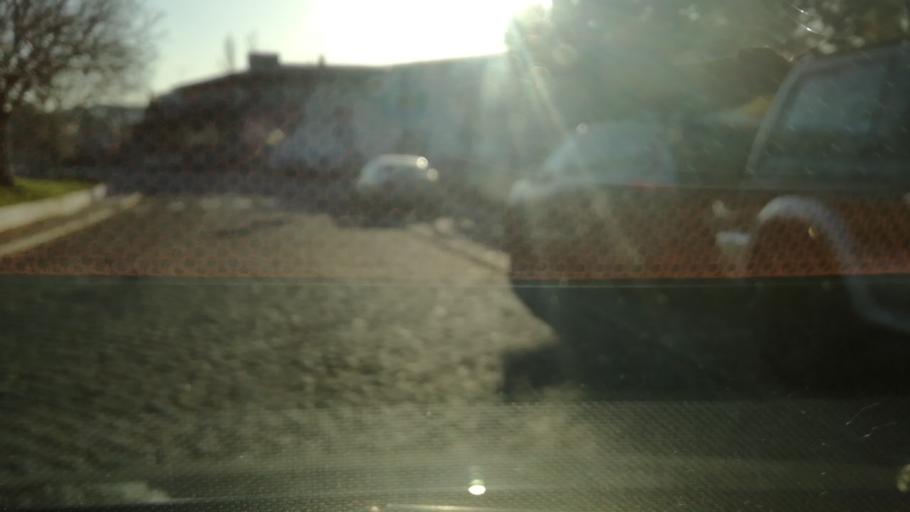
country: PT
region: Braga
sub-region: Vila Nova de Famalicao
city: Ferreiros
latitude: 41.3408
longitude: -8.5263
